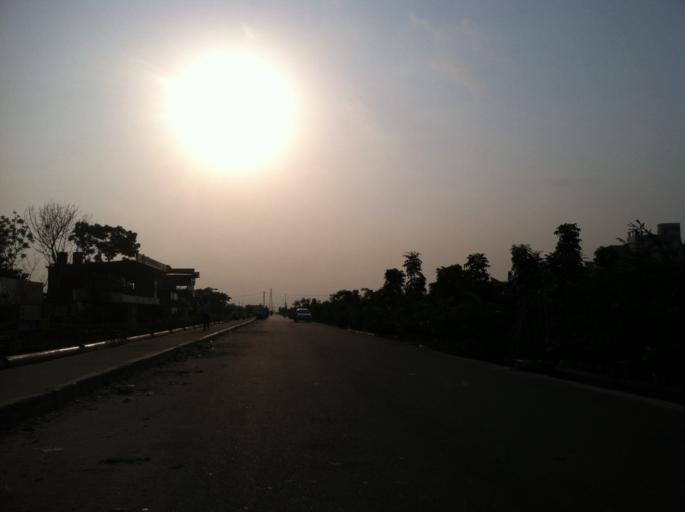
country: BD
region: Dhaka
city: Tungi
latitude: 23.8271
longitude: 90.4304
